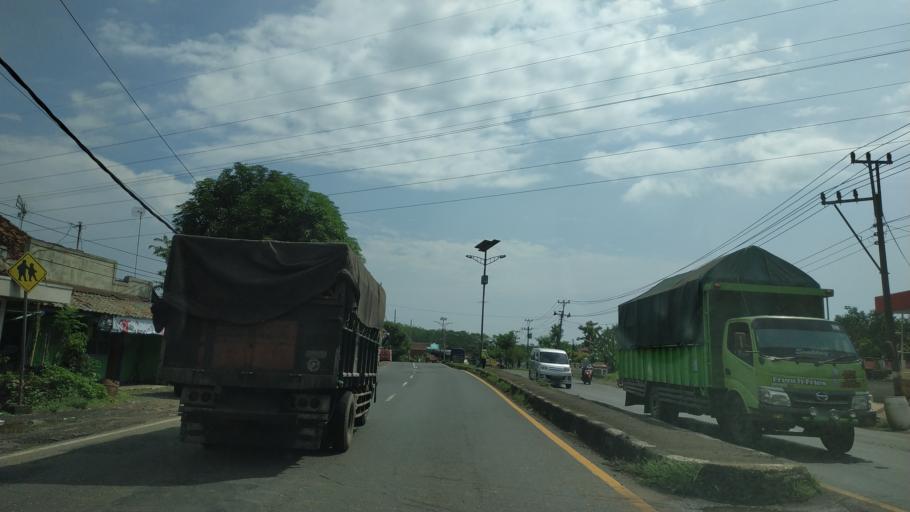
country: ID
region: Central Java
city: Pekalongan
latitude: -6.9474
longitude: 109.8085
